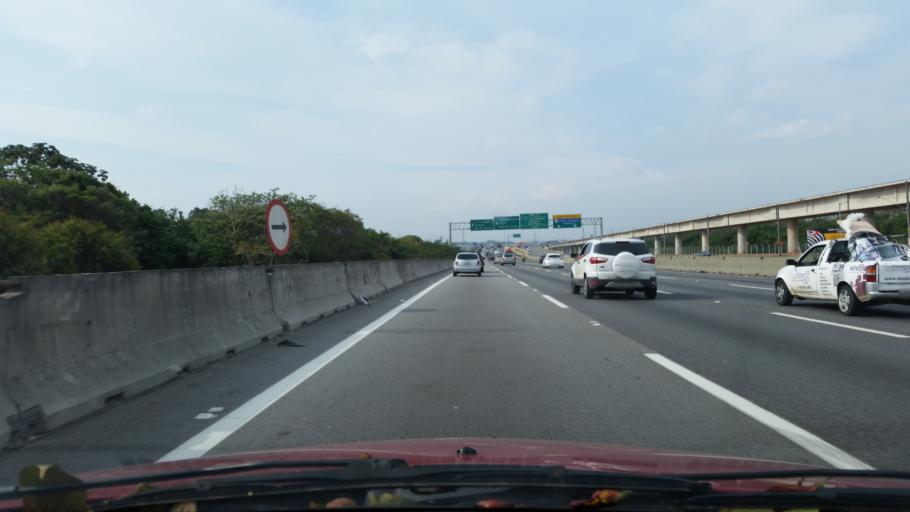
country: BR
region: Sao Paulo
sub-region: Guarulhos
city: Guarulhos
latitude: -23.4835
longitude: -46.5047
